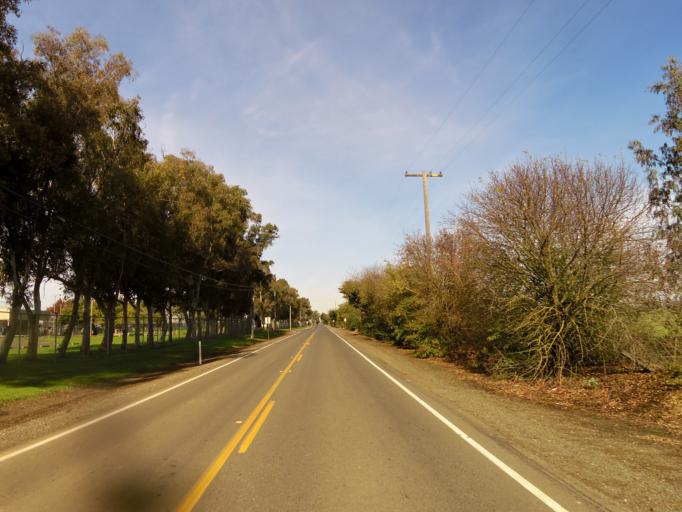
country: US
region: California
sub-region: San Joaquin County
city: Thornton
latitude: 38.3055
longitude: -121.4200
